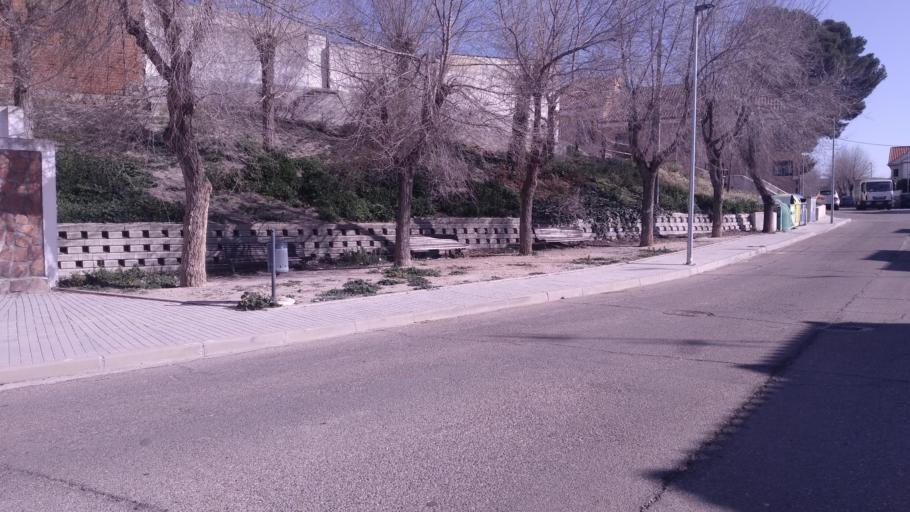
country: ES
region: Castille-La Mancha
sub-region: Province of Toledo
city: Esquivias
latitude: 40.1012
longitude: -3.7620
